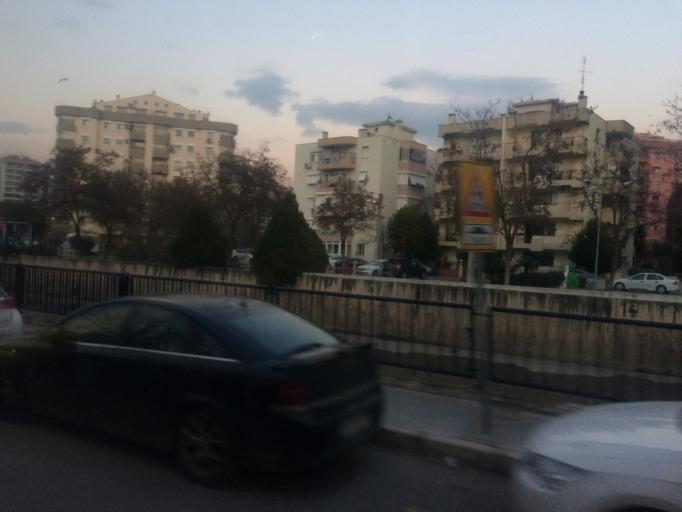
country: TR
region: Izmir
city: Karsiyaka
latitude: 38.4627
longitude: 27.0962
